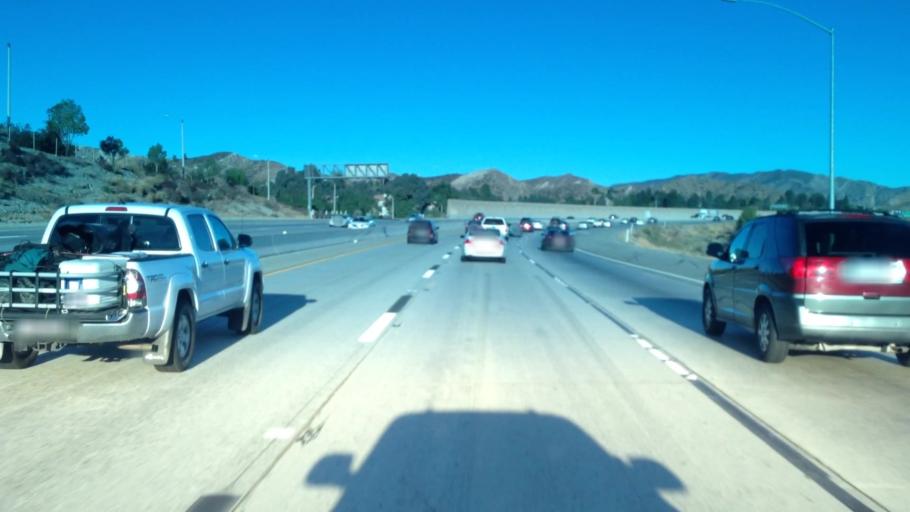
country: US
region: California
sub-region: Los Angeles County
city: Agua Dulce
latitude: 34.4268
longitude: -118.4200
